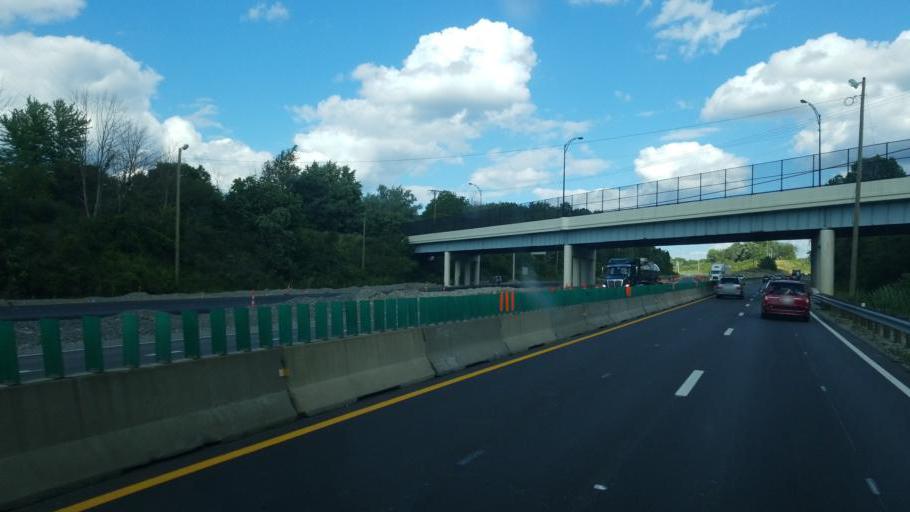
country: US
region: Ohio
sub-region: Trumbull County
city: Girard
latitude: 41.1480
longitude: -80.6862
